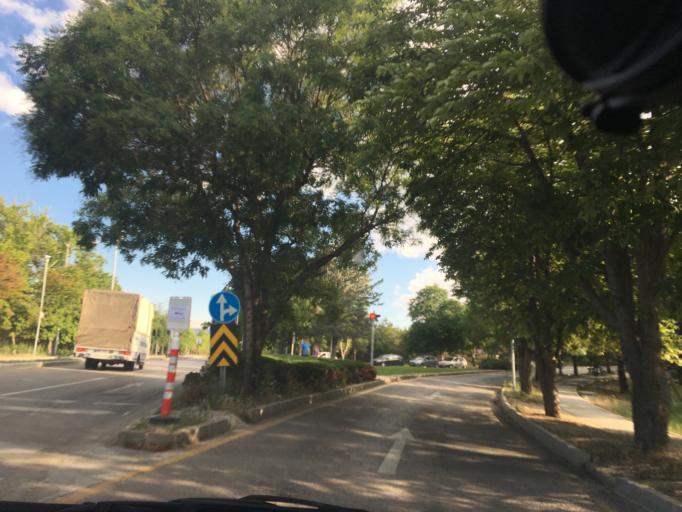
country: TR
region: Ankara
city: Ankara
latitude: 39.9018
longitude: 32.7832
